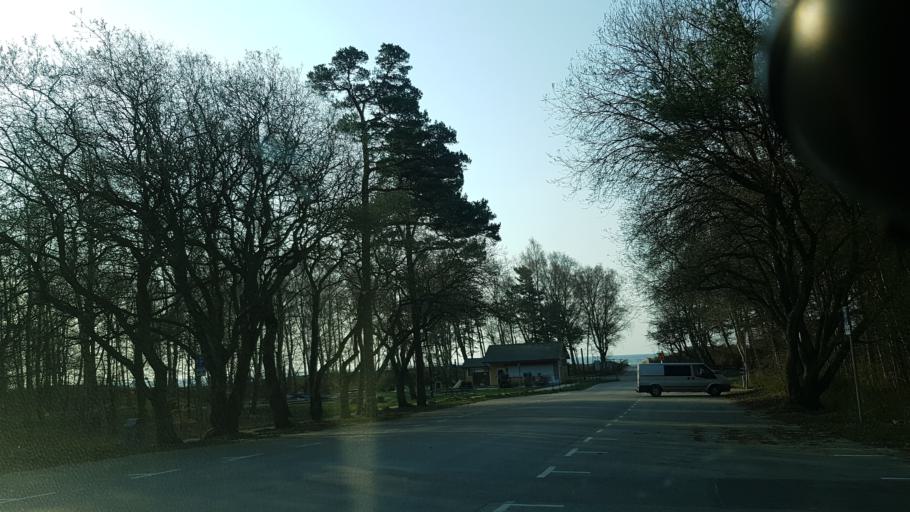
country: SE
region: Skane
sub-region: Ystads Kommun
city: Ystad
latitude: 55.4319
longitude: 13.8653
